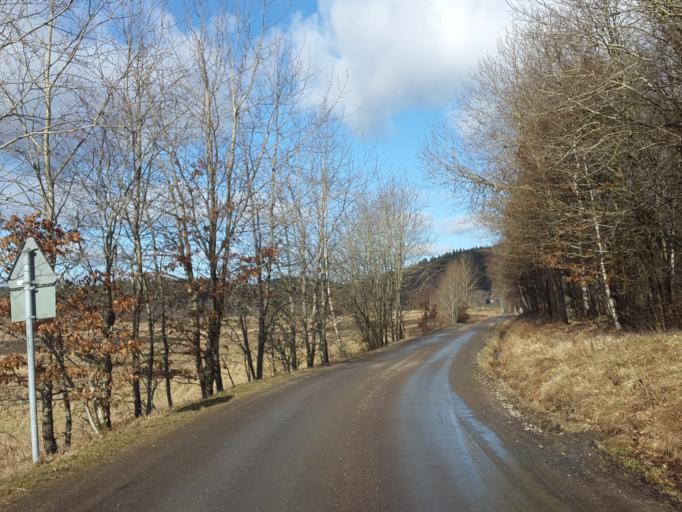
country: SE
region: Vaestra Goetaland
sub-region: Lerums Kommun
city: Olstorp
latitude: 57.8281
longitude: 12.2209
